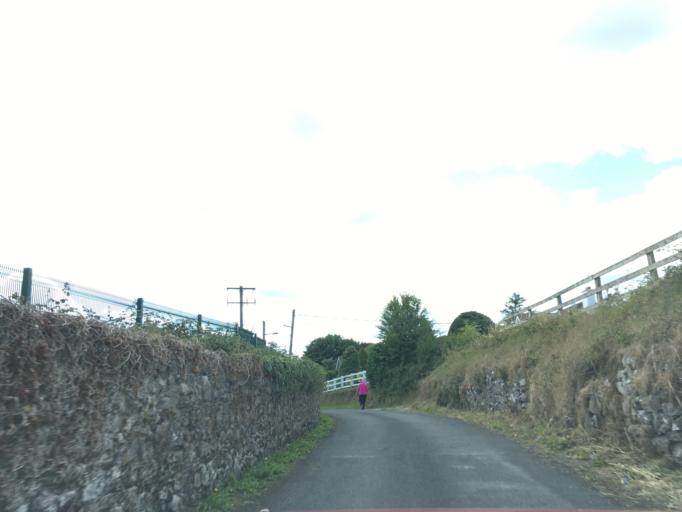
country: IE
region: Munster
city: Cashel
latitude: 52.5202
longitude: -7.8818
